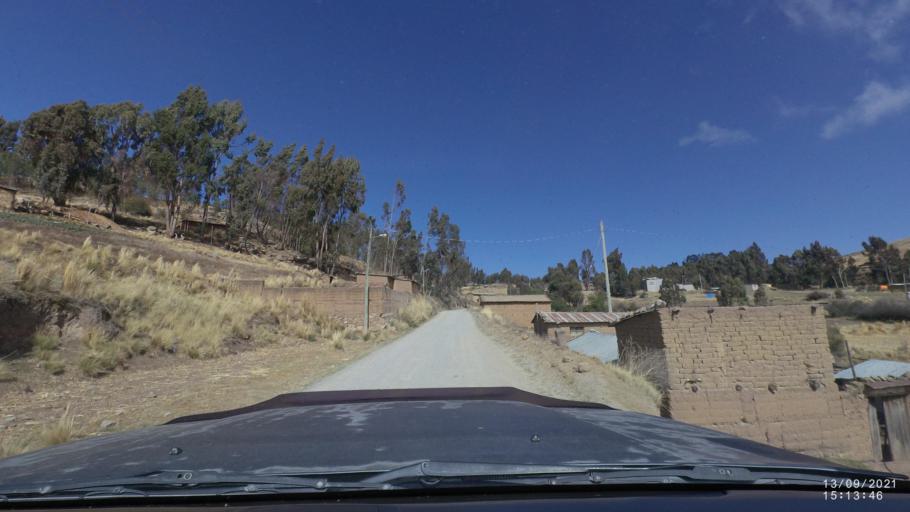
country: BO
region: Cochabamba
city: Colomi
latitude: -17.3621
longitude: -65.8017
